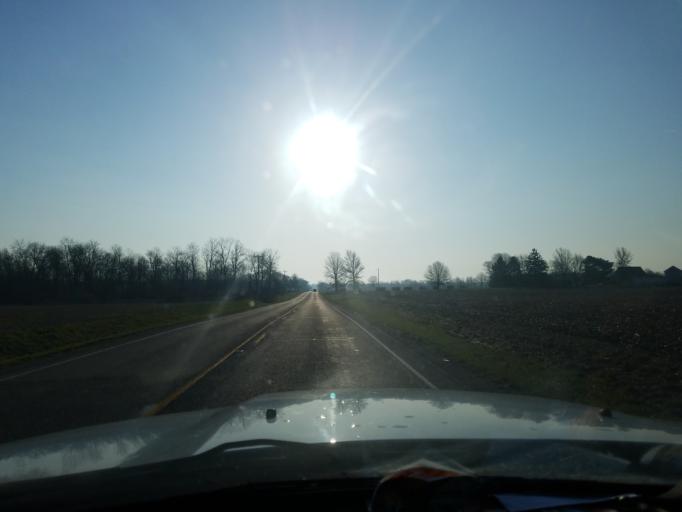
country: US
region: Indiana
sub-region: Vigo County
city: Seelyville
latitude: 39.3903
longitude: -87.2564
